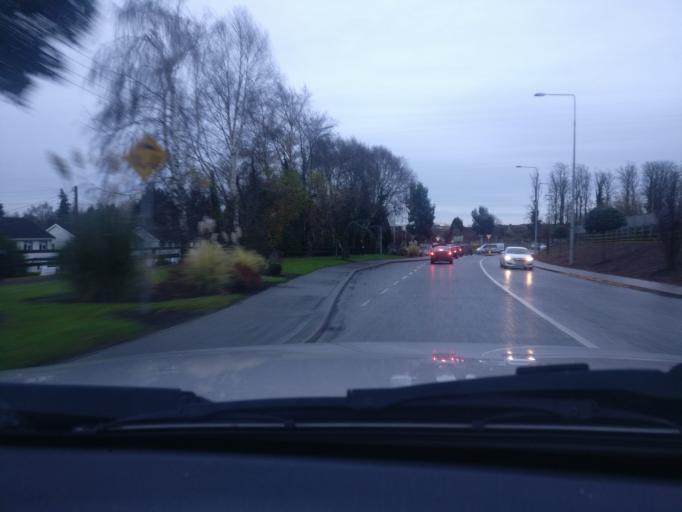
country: IE
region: Leinster
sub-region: An Mhi
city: Navan
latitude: 53.6547
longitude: -6.7002
